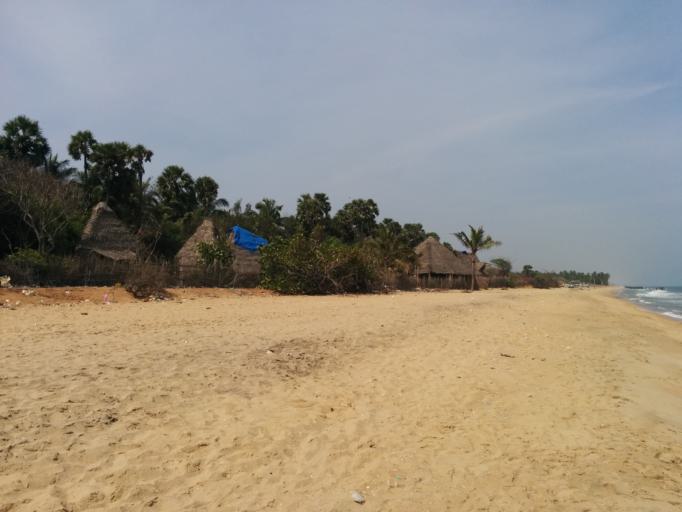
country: IN
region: Tamil Nadu
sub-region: Villupuram
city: Auroville
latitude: 11.9849
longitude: 79.8489
